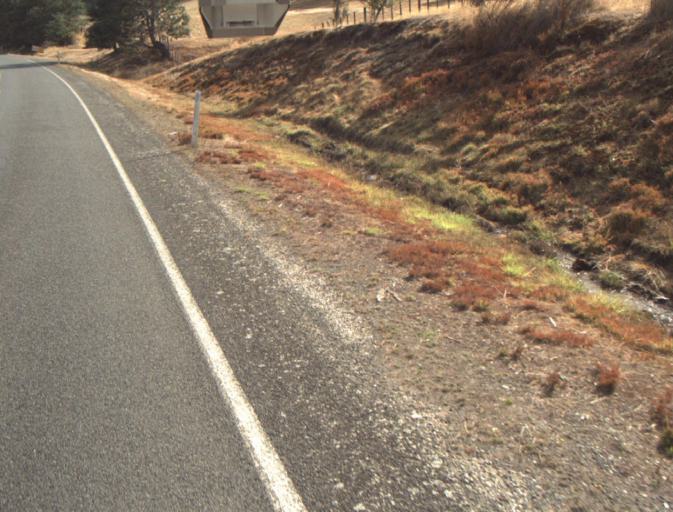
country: AU
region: Tasmania
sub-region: Launceston
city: Mayfield
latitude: -41.2910
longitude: 147.2167
